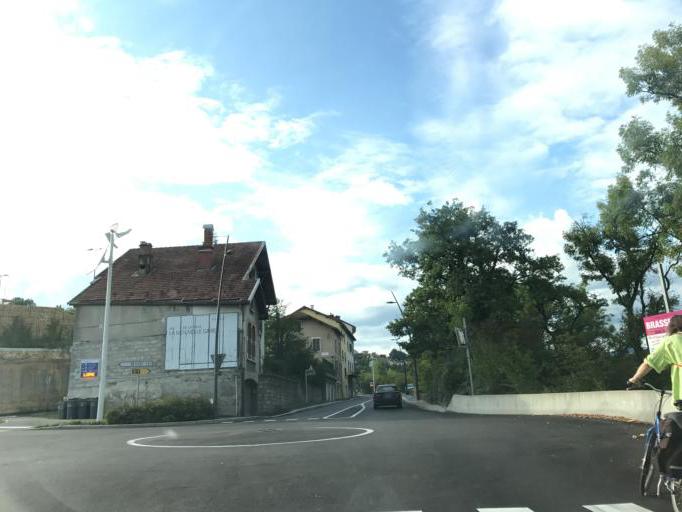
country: FR
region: Rhone-Alpes
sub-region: Departement de l'Ain
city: Bellegarde-sur-Valserine
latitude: 46.1116
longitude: 5.8275
